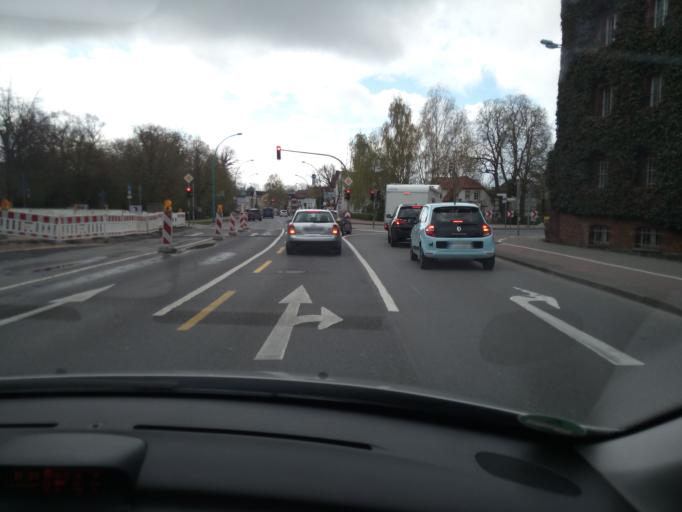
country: DE
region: Mecklenburg-Vorpommern
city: Neubrandenburg
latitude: 53.5572
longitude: 13.2539
